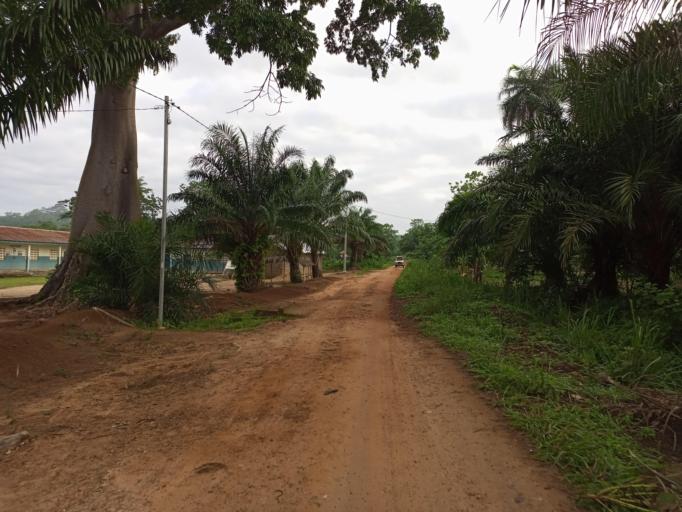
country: SL
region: Eastern Province
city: Pendembu
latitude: 8.1136
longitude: -10.6915
